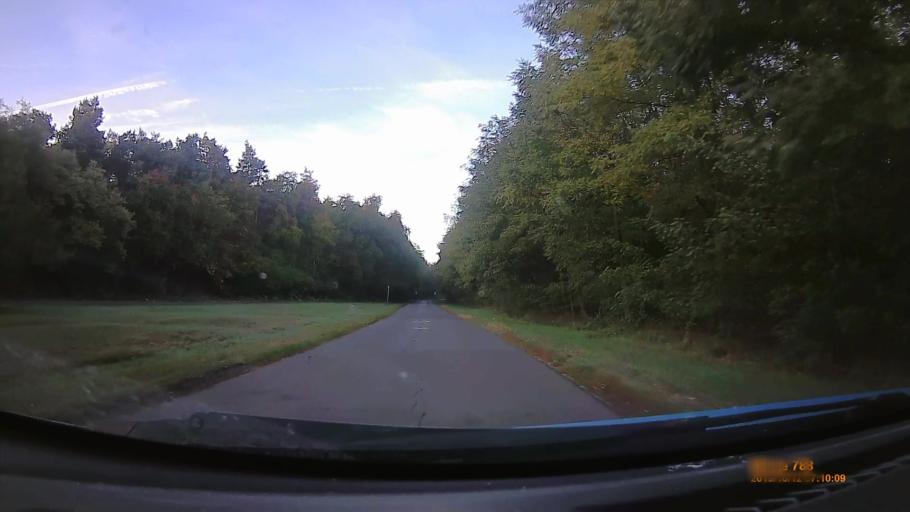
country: HU
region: Hajdu-Bihar
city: Mikepercs
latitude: 47.4644
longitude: 21.6779
